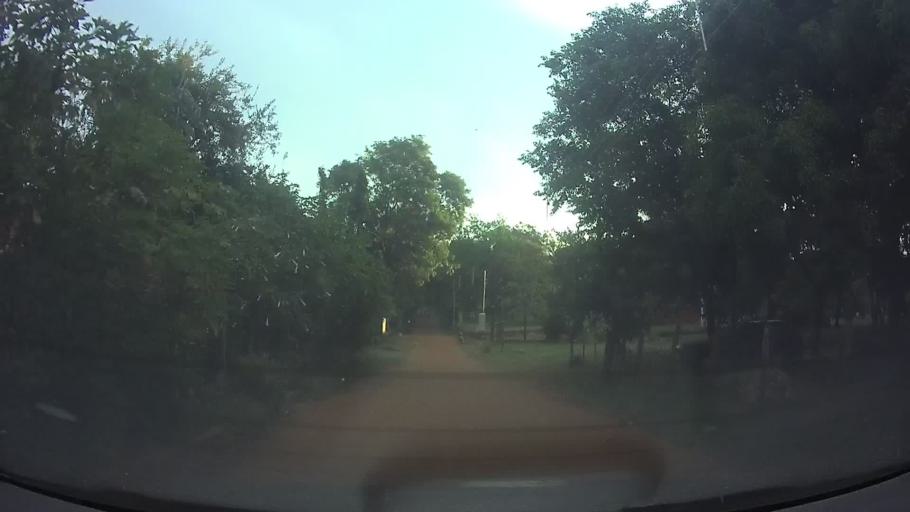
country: PY
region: Central
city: Limpio
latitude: -25.2412
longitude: -57.4477
